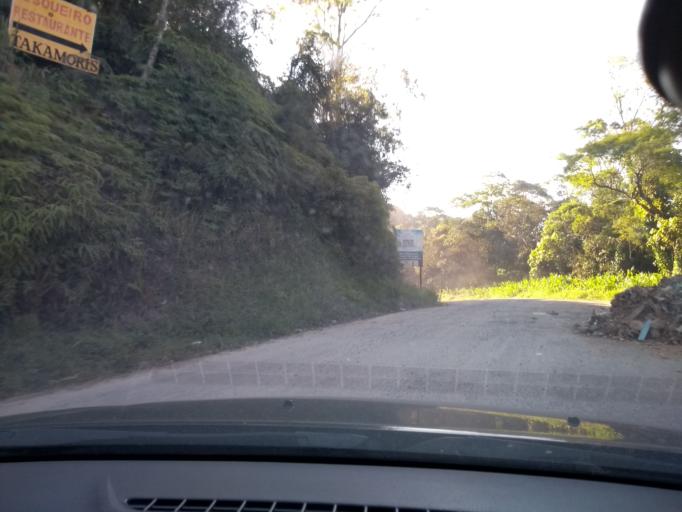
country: BR
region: Sao Paulo
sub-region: Rio Grande Da Serra
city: Rio Grande da Serra
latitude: -23.7790
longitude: -46.4851
